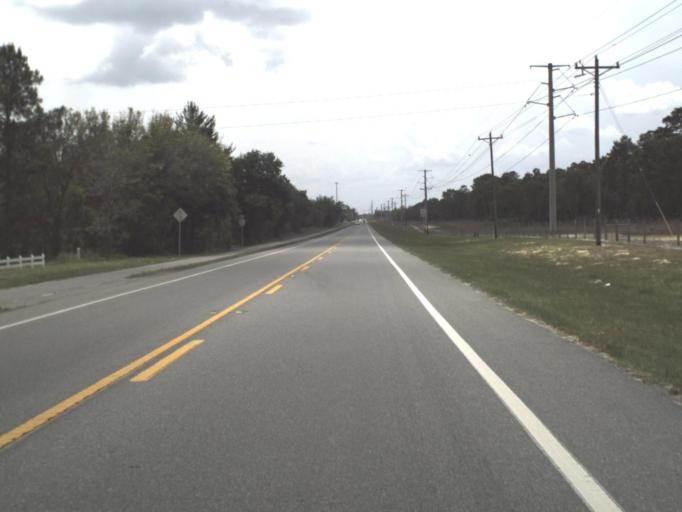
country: US
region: Florida
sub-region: Clay County
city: Keystone Heights
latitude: 29.8186
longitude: -81.9978
